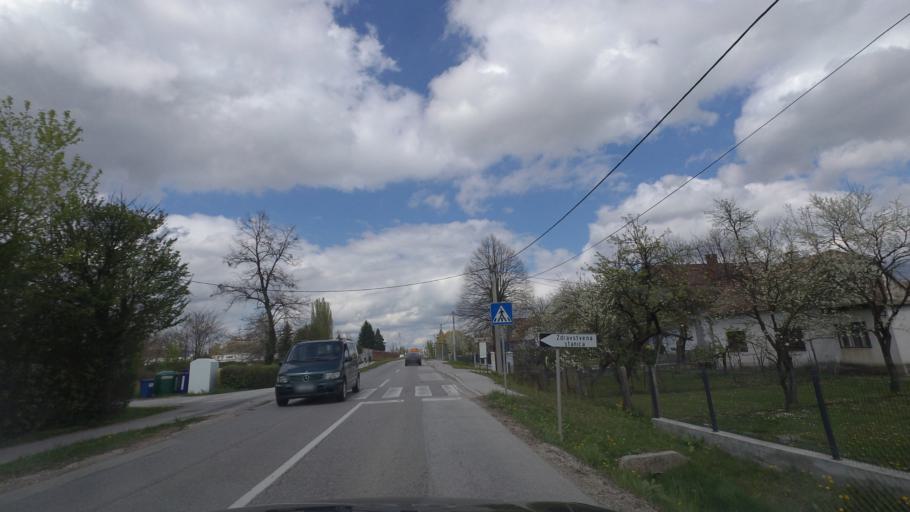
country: HR
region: Zagrebacka
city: Kerestinec
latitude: 45.7616
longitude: 15.8063
